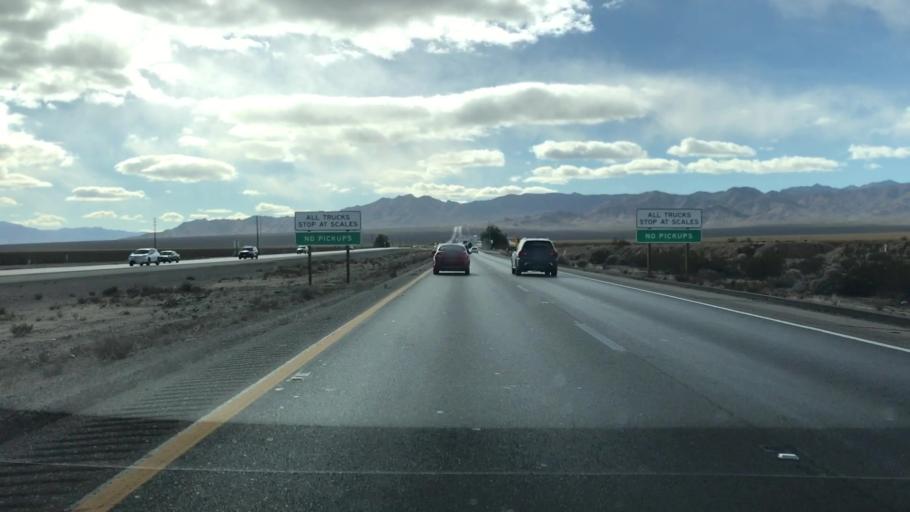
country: US
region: Nevada
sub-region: Clark County
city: Sandy Valley
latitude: 35.5395
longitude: -115.4205
